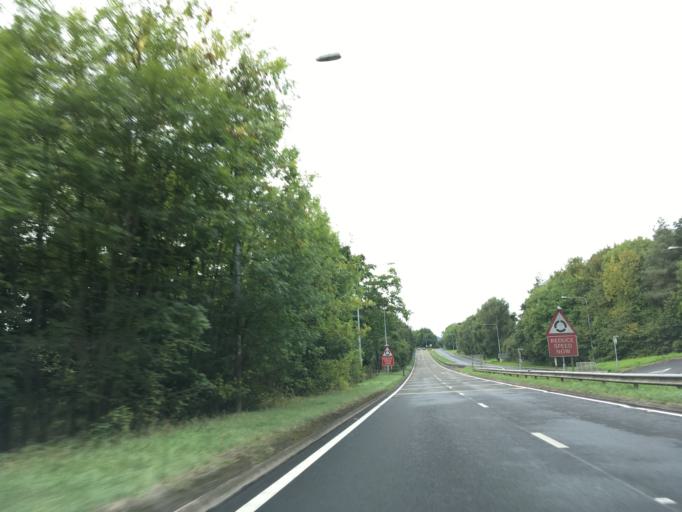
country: GB
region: Wales
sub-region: Monmouthshire
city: Llanarth
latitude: 51.7672
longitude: -2.8487
